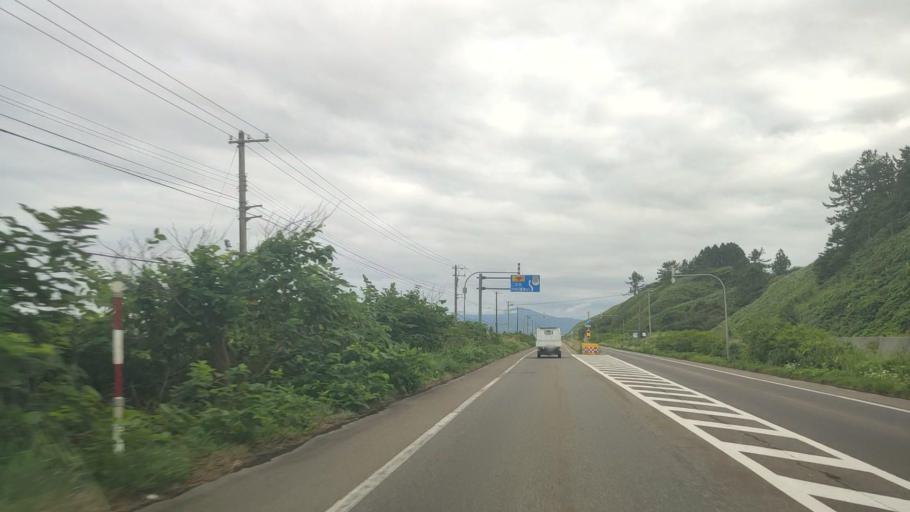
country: JP
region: Hokkaido
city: Niseko Town
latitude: 42.3333
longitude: 140.2786
